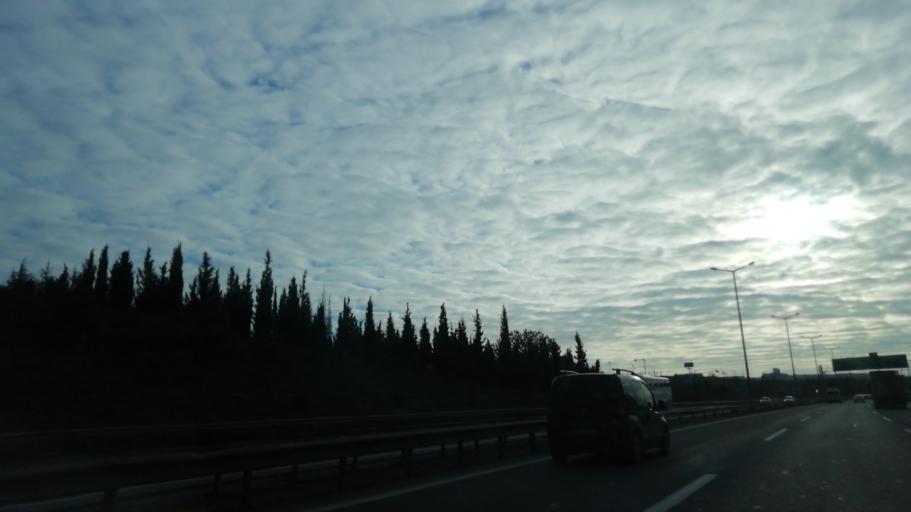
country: TR
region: Kocaeli
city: Balcik
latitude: 40.8740
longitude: 29.3918
